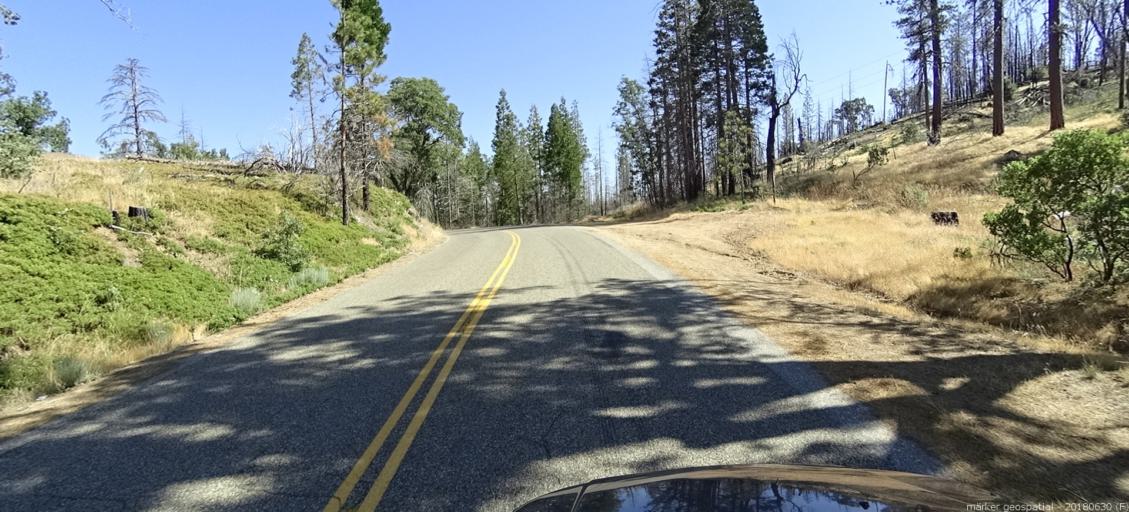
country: US
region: California
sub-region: Fresno County
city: Auberry
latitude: 37.2535
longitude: -119.3493
